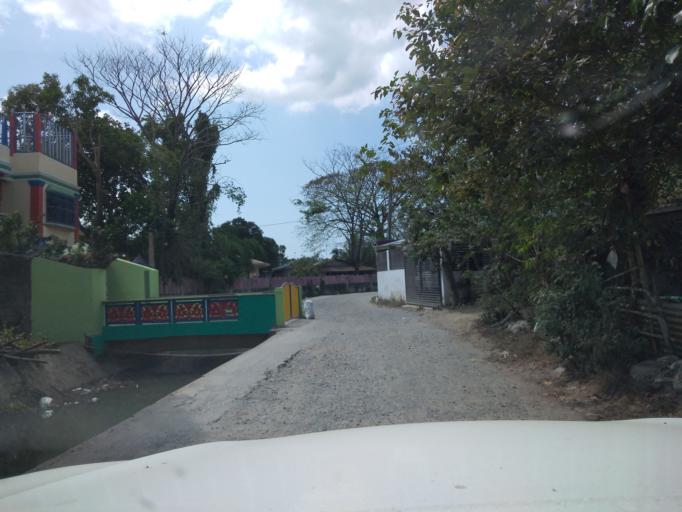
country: PH
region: Central Luzon
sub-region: Province of Pampanga
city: Bahay Pare
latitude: 15.0353
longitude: 120.8726
